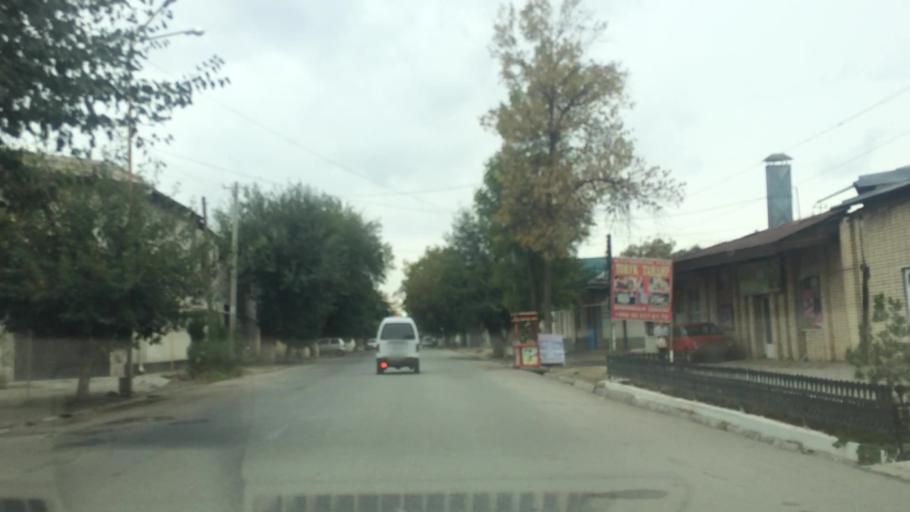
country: UZ
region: Samarqand
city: Samarqand
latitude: 39.6611
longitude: 66.9751
